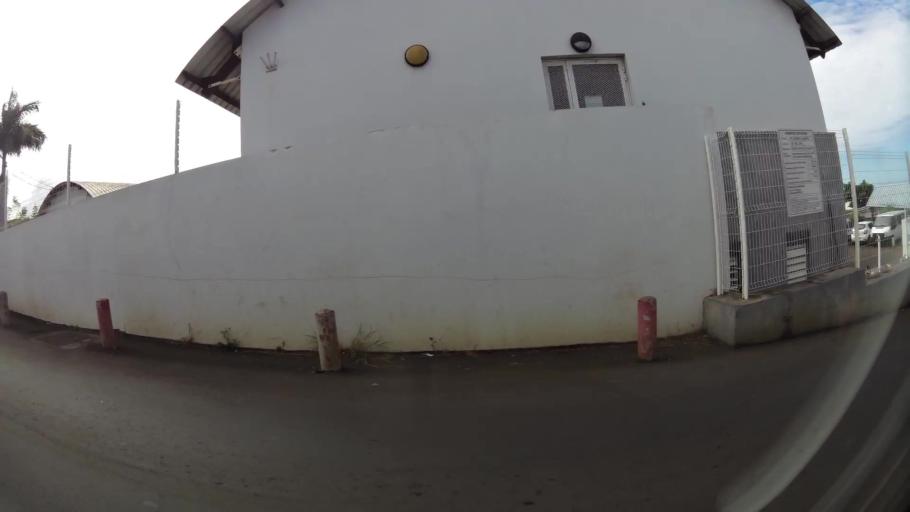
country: YT
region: Mamoudzou
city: Mamoudzou
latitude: -12.7789
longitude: 45.2264
